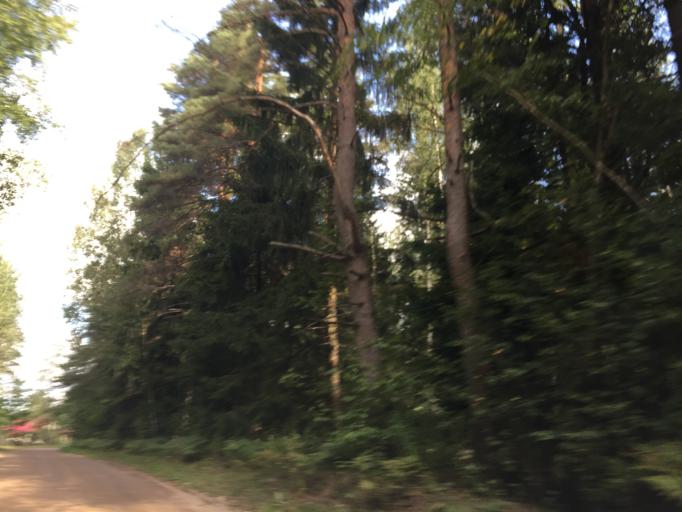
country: LV
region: Incukalns
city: Vangazi
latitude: 57.0895
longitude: 24.5635
